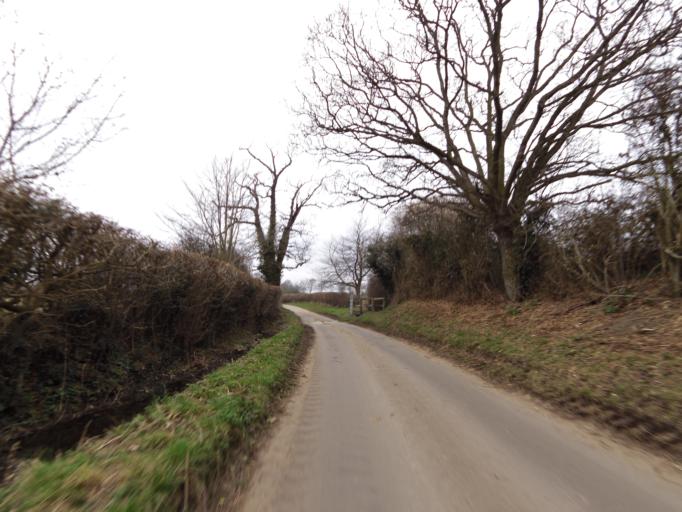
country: GB
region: England
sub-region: Suffolk
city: Framlingham
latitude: 52.2456
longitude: 1.4032
